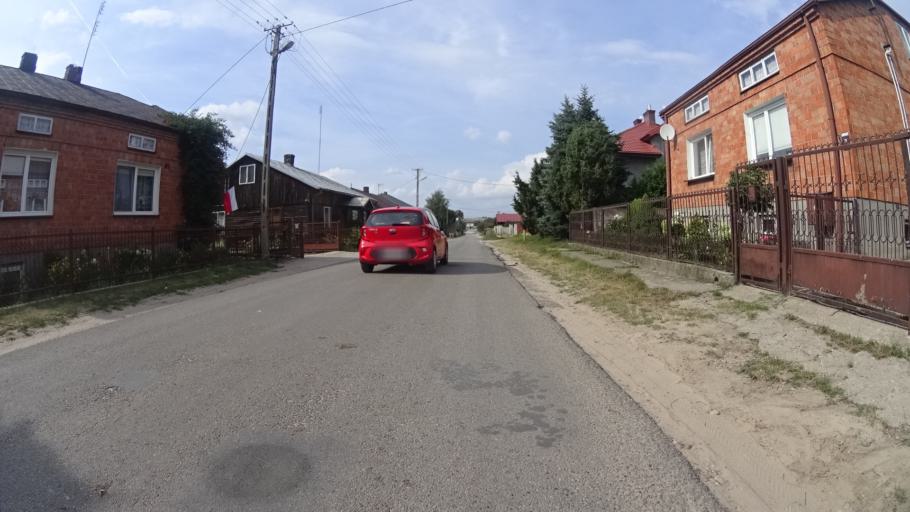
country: PL
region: Masovian Voivodeship
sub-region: Powiat bialobrzeski
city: Wysmierzyce
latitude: 51.6535
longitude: 20.7839
